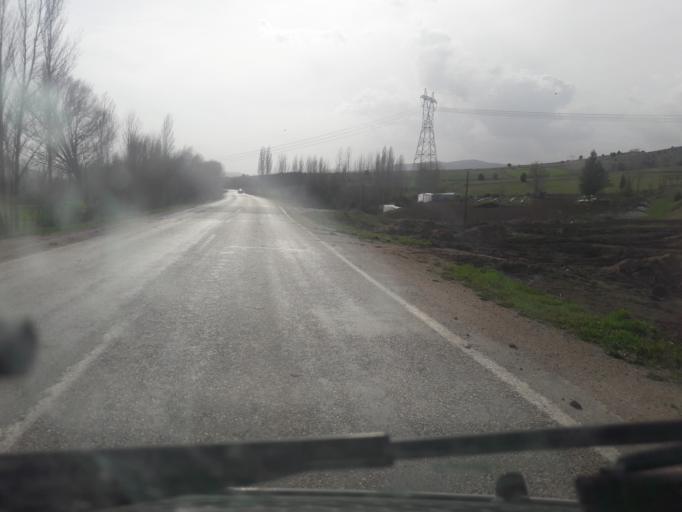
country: TR
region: Gumushane
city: Kelkit
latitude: 40.1305
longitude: 39.3641
